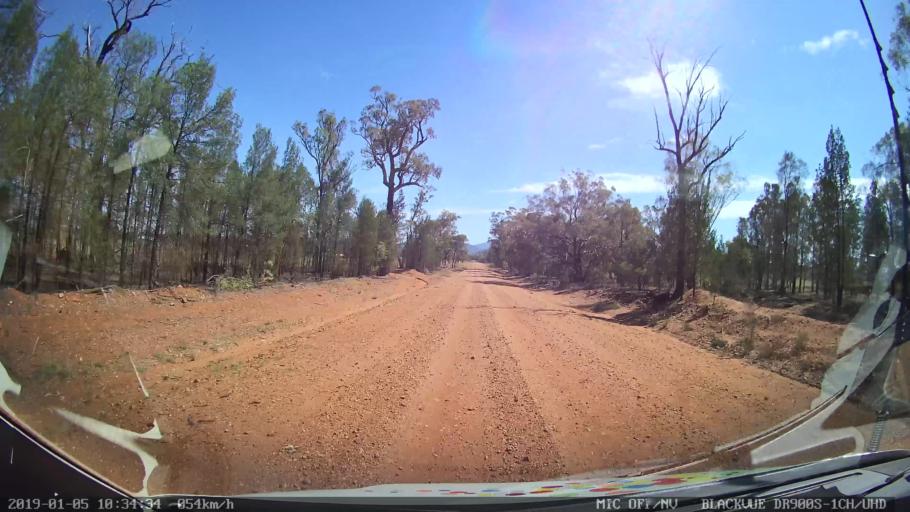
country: AU
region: New South Wales
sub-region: Gilgandra
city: Gilgandra
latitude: -31.4973
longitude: 148.9292
